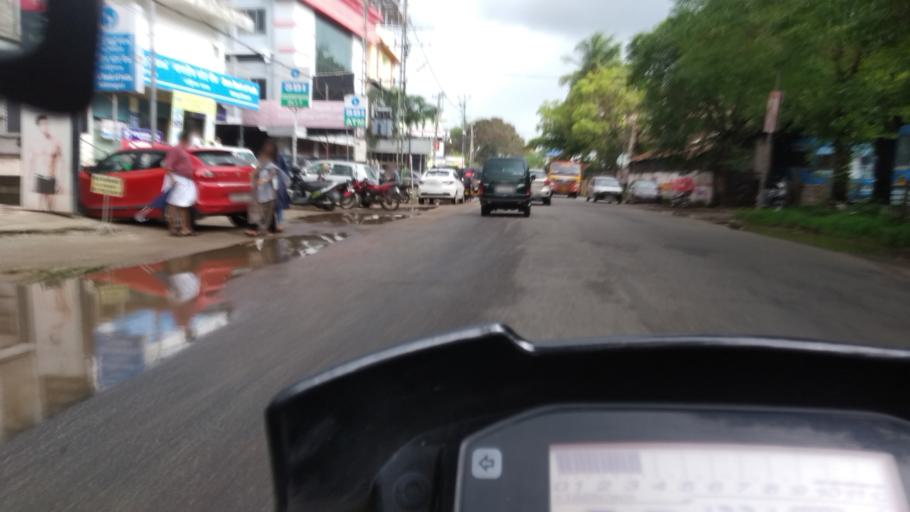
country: IN
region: Kerala
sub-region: Thiruvananthapuram
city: Attingal
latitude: 8.7048
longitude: 76.8149
